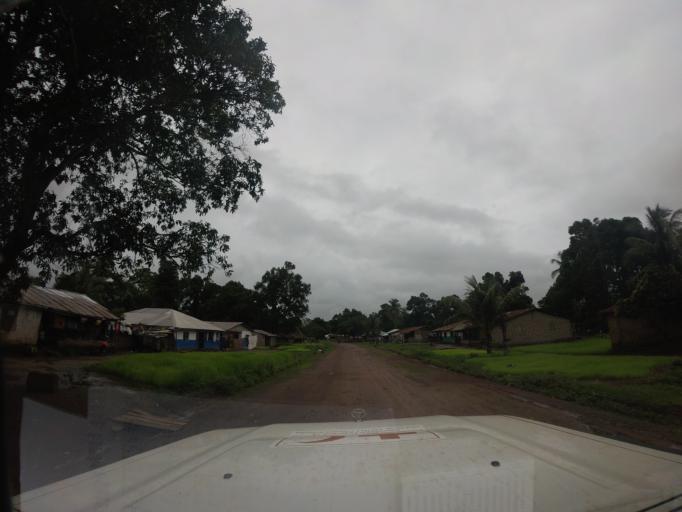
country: SL
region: Northern Province
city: Kambia
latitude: 9.1827
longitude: -12.8766
